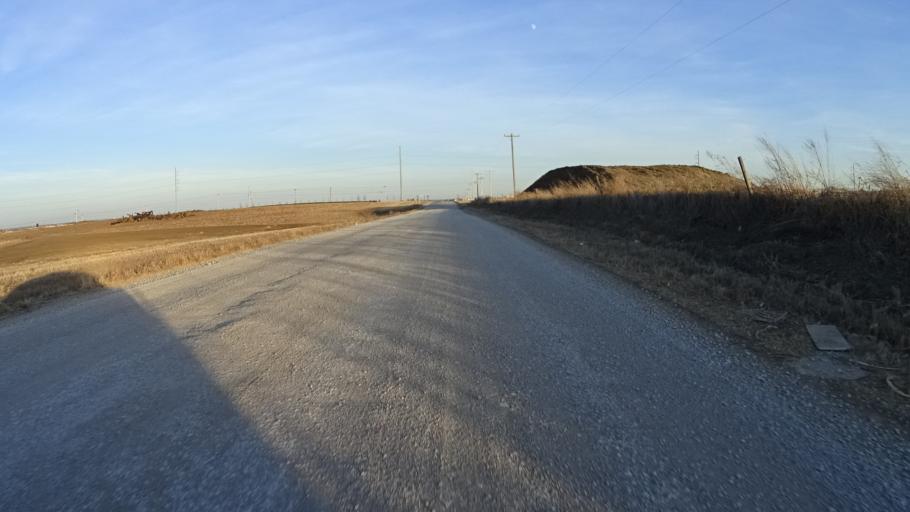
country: US
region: Nebraska
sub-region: Sarpy County
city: Papillion
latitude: 41.1326
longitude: -96.0946
